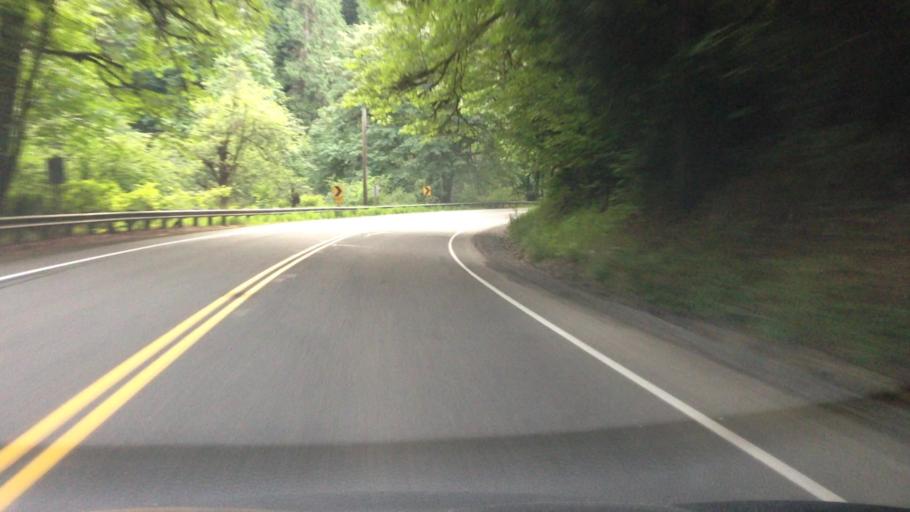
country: US
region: Washington
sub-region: King County
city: Duvall
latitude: 47.7442
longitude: -122.0120
